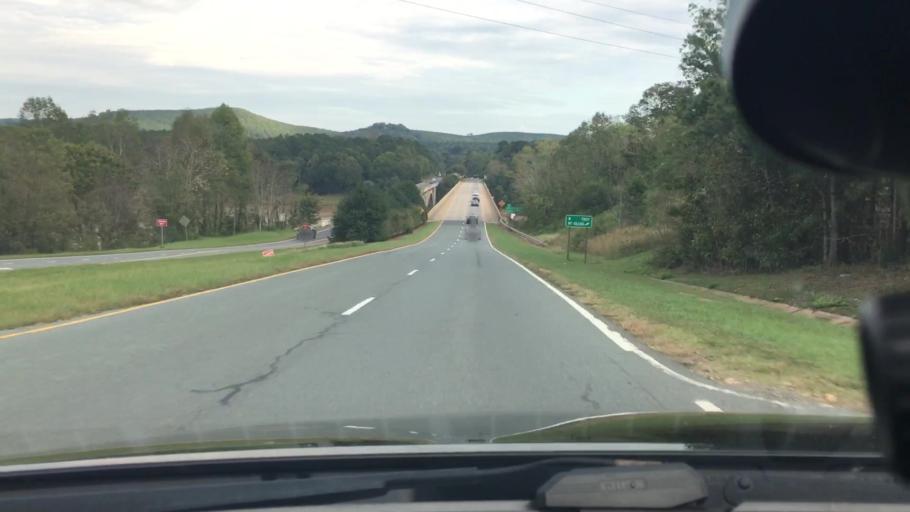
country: US
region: North Carolina
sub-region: Stanly County
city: Norwood
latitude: 35.3092
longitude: -80.0831
